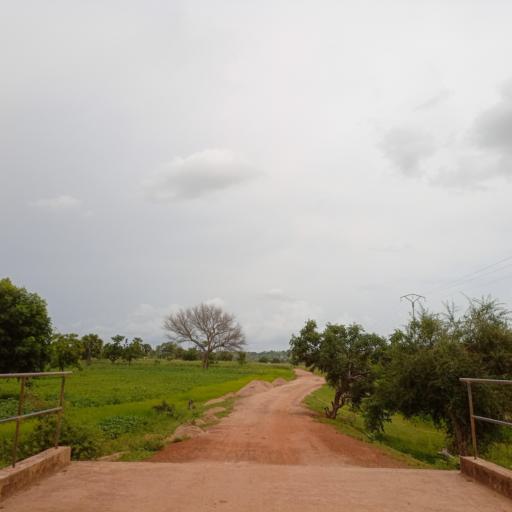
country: TG
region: Savanes
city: Dapaong
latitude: 10.8087
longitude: 0.0274
